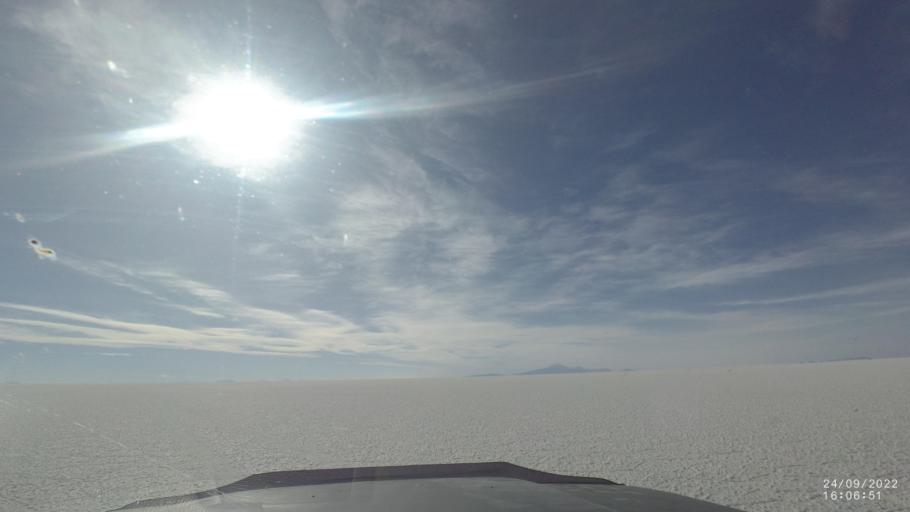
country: BO
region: Potosi
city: Colchani
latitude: -20.3033
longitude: -67.2978
